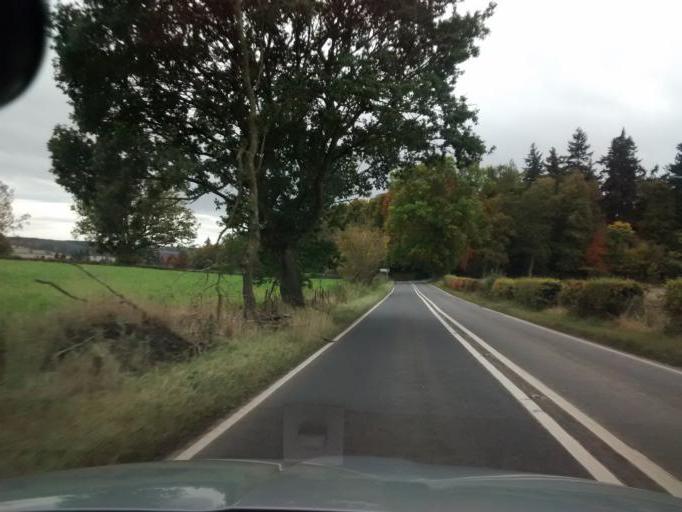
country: GB
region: Scotland
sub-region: Perth and Kinross
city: Blairgowrie
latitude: 56.5367
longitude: -3.3624
